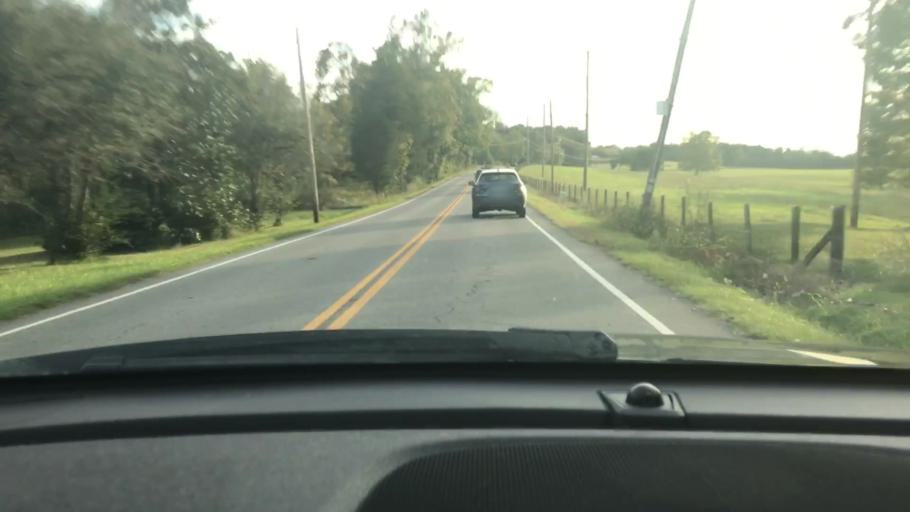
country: US
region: Tennessee
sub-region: Dickson County
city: Charlotte
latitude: 36.2323
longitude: -87.2501
